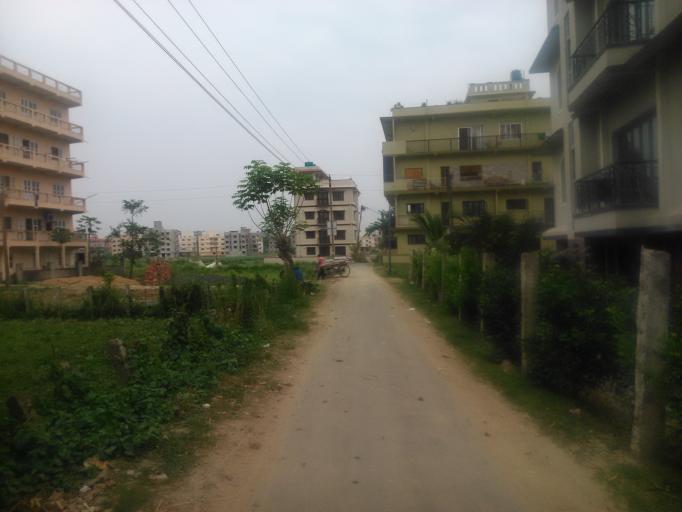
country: IN
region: West Bengal
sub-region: Nadia
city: Navadwip
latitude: 23.4327
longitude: 88.3940
